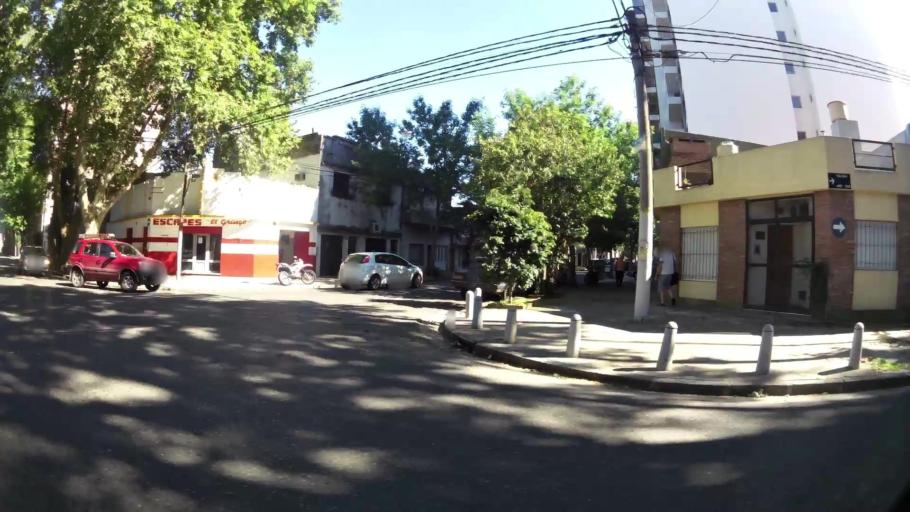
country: AR
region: Santa Fe
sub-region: Departamento de Rosario
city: Rosario
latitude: -32.9468
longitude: -60.6796
